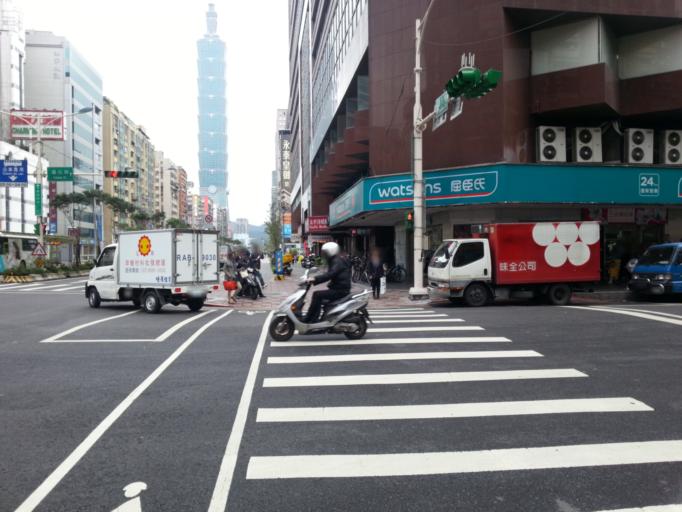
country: TW
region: Taipei
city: Taipei
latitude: 25.0331
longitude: 121.5542
